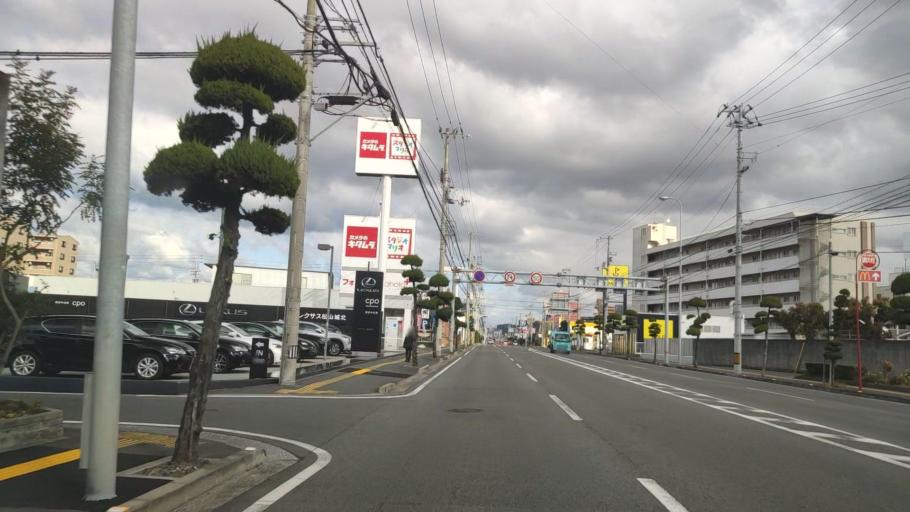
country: JP
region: Ehime
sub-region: Shikoku-chuo Shi
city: Matsuyama
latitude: 33.8568
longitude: 132.7484
